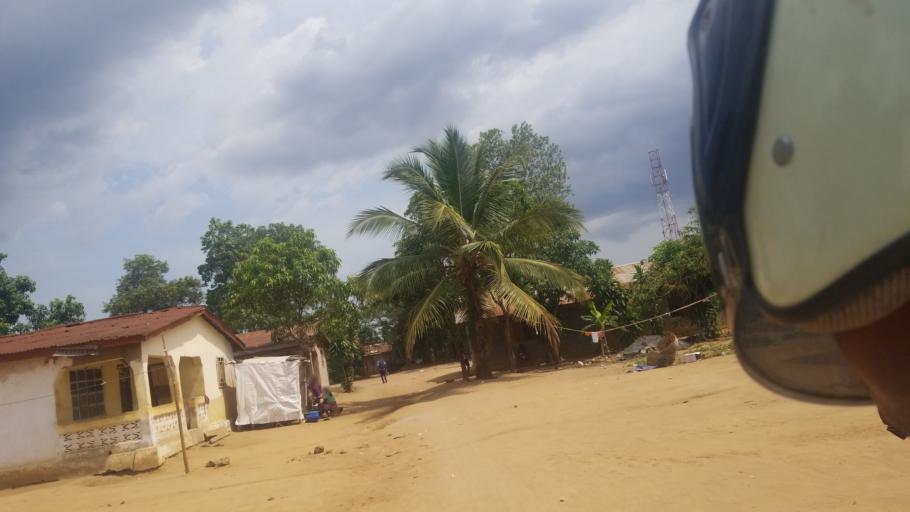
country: SL
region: Western Area
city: Waterloo
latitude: 8.3189
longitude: -13.0466
